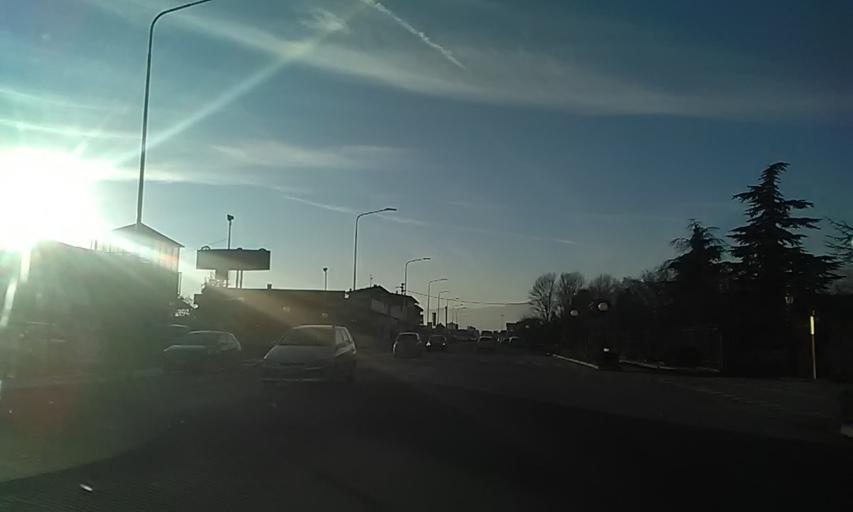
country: IT
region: Piedmont
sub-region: Provincia di Biella
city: Cerreto Castello
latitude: 45.5647
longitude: 8.1606
